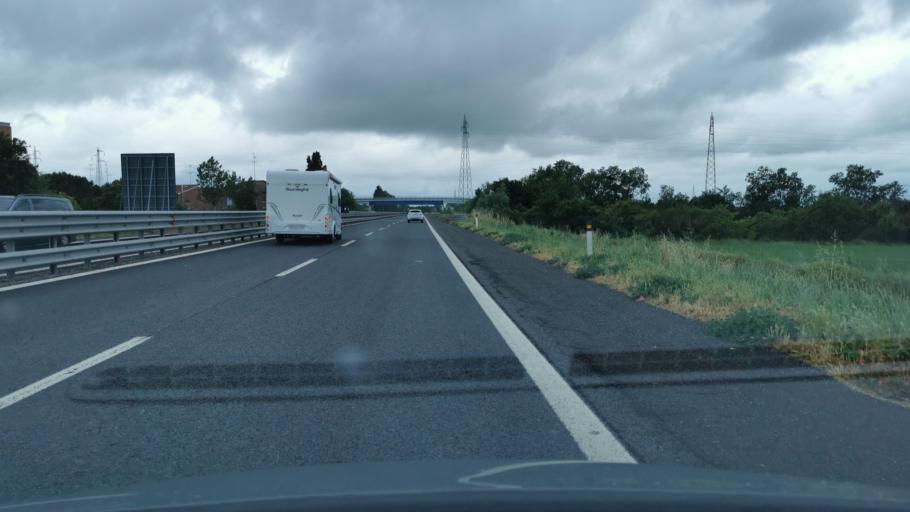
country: IT
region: Emilia-Romagna
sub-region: Provincia di Ravenna
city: Fornace Zarattini
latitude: 44.4230
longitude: 12.1461
